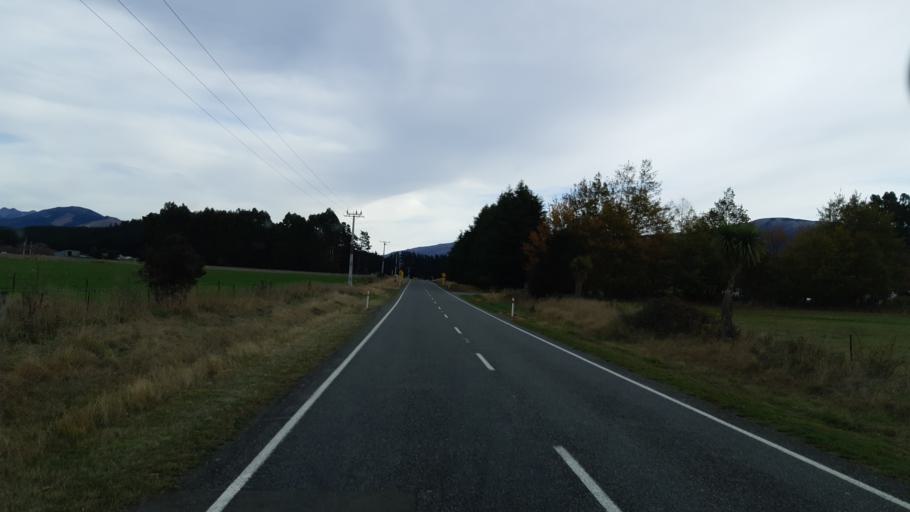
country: NZ
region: Tasman
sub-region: Tasman District
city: Brightwater
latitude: -41.6564
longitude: 173.2429
